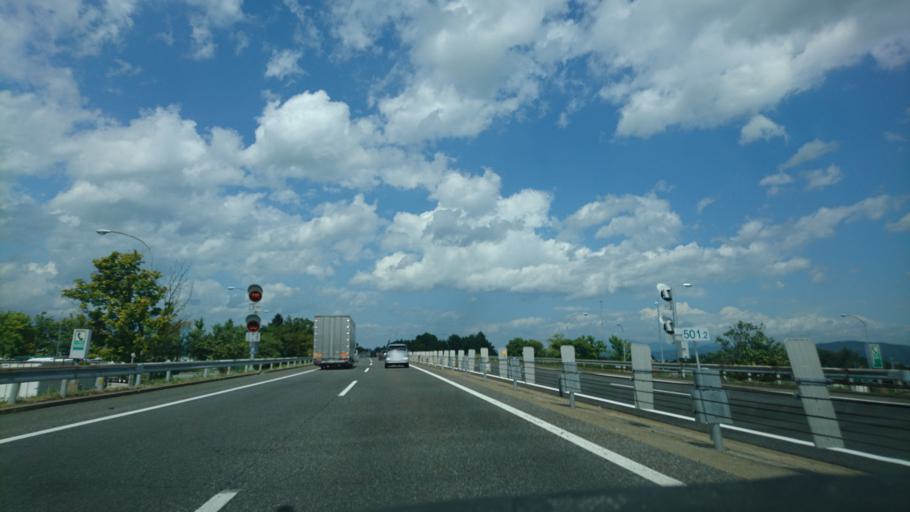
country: JP
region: Iwate
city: Morioka-shi
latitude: 39.6182
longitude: 141.1297
